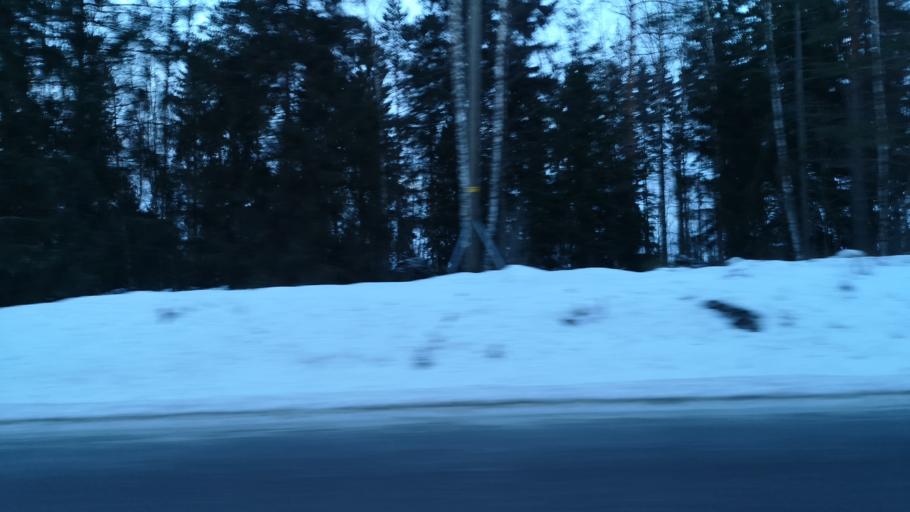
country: FI
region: Uusimaa
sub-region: Raaseporin
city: Inga
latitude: 60.0857
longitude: 23.9444
